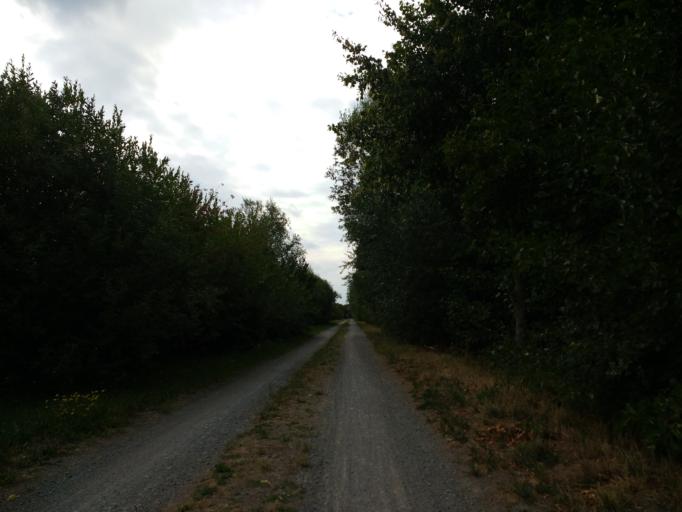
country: DE
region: Lower Saxony
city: Weyhausen
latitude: 52.4262
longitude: 10.7251
